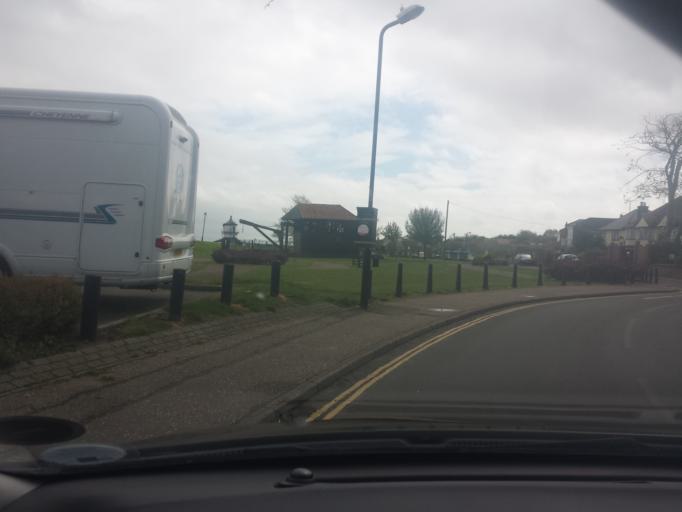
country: GB
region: England
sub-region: Essex
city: Harwich
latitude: 51.9454
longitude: 1.2898
